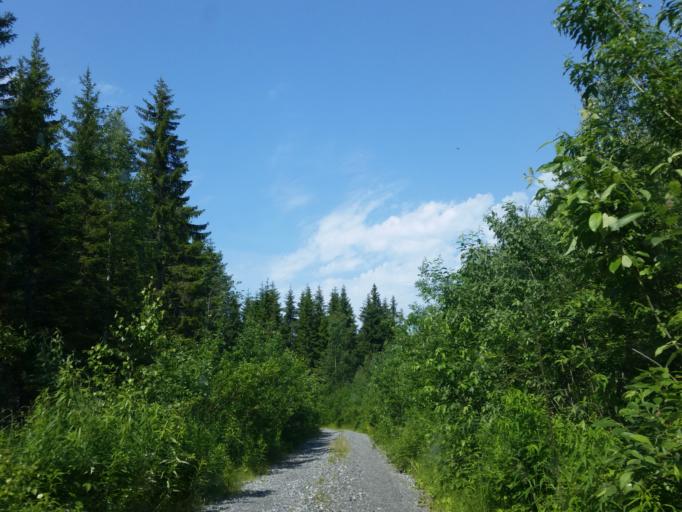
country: FI
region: Northern Savo
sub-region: Ylae-Savo
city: Keitele
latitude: 63.1040
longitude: 26.5404
